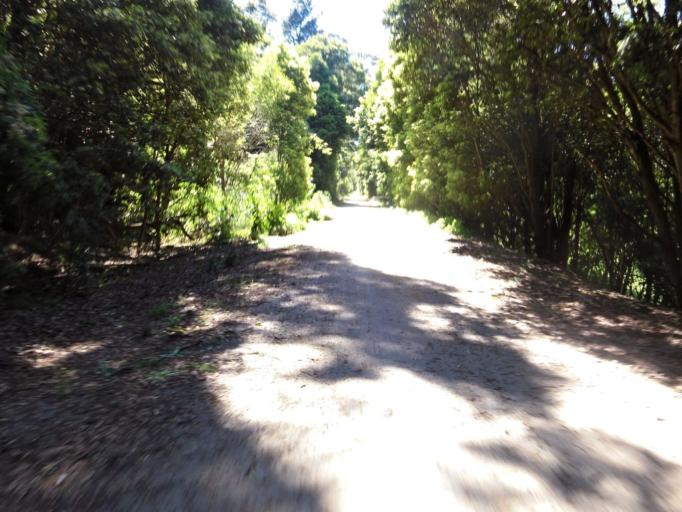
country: AU
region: Victoria
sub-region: Latrobe
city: Morwell
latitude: -38.6792
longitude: 146.1592
